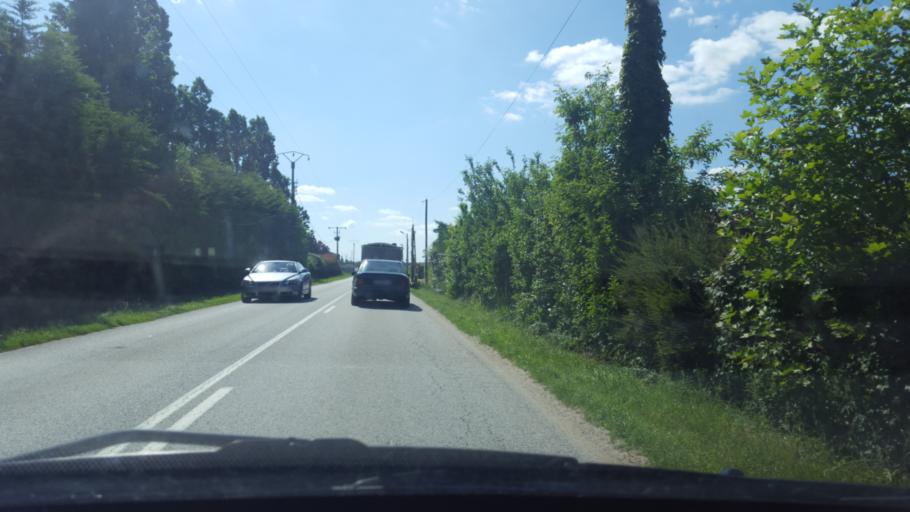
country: FR
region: Pays de la Loire
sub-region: Departement de la Loire-Atlantique
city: La Chevroliere
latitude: 47.0615
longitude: -1.5740
